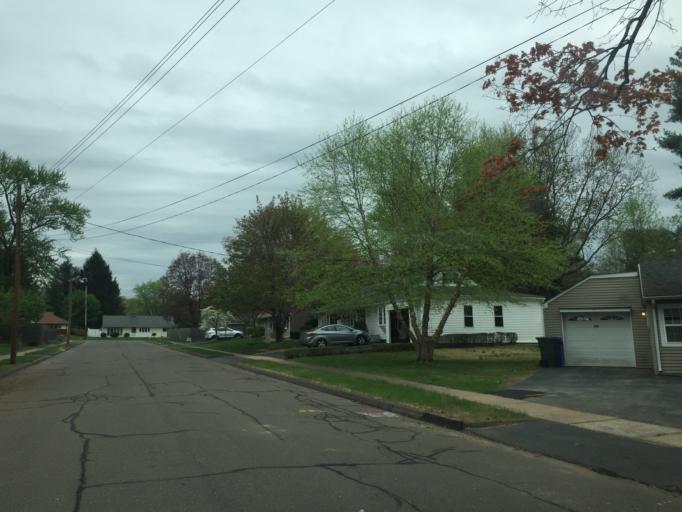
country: US
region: Connecticut
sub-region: Hartford County
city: Glastonbury
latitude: 41.7330
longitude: -72.5896
